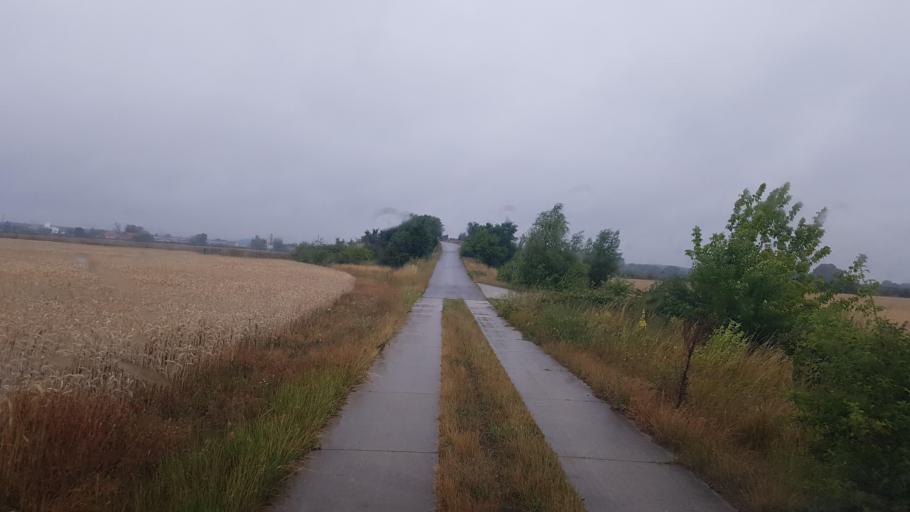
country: DE
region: Brandenburg
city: Trebbin
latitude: 52.1895
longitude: 13.2562
